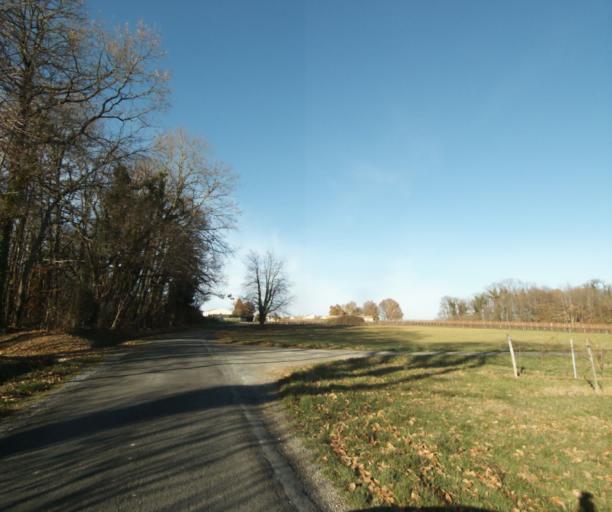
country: FR
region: Poitou-Charentes
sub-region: Departement de la Charente-Maritime
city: Burie
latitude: 45.7766
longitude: -0.4320
